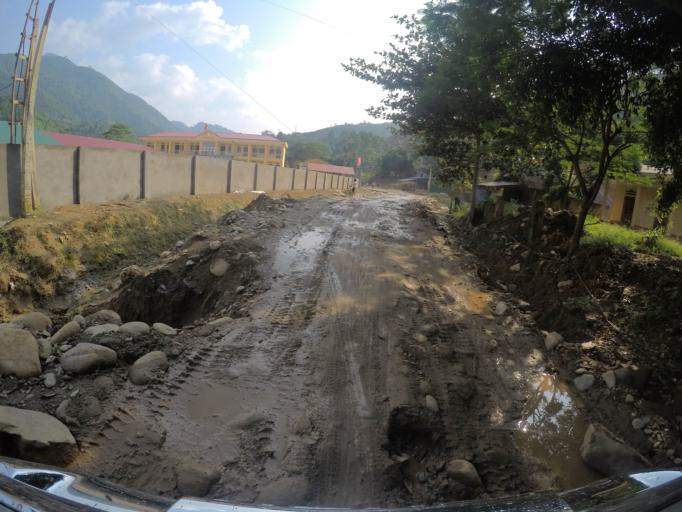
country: VN
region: Yen Bai
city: Co Phuc
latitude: 21.7761
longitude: 104.6424
